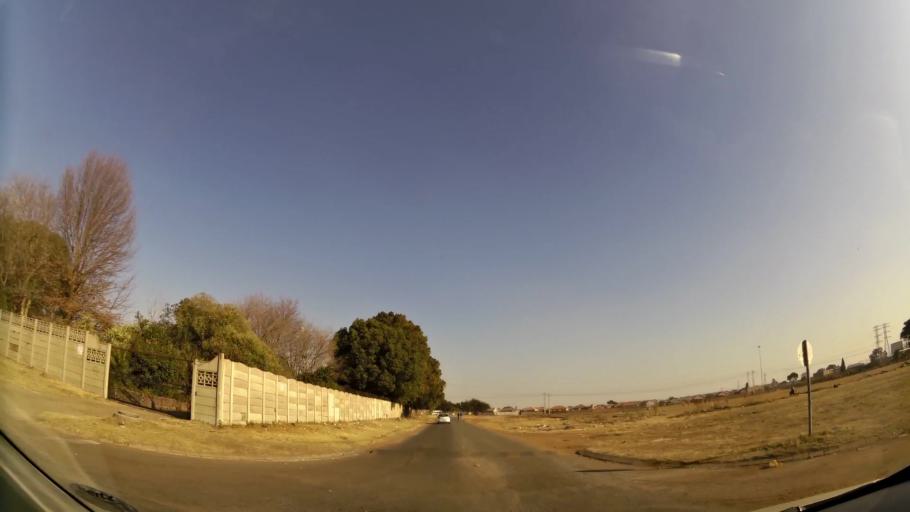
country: ZA
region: Gauteng
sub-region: West Rand District Municipality
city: Randfontein
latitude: -26.1858
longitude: 27.6999
